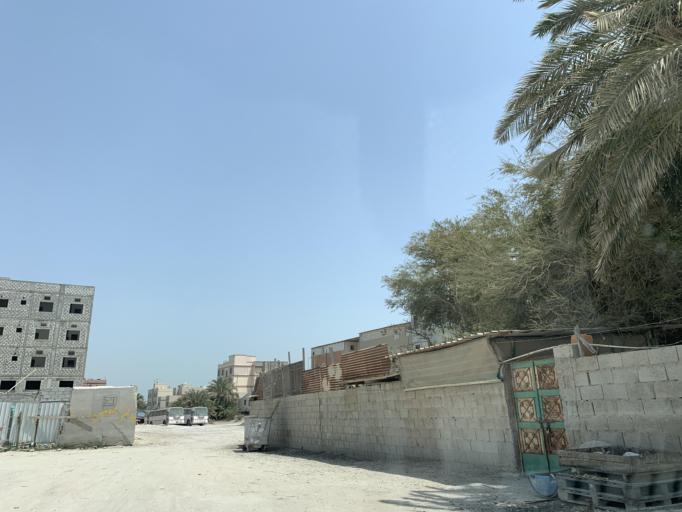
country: BH
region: Northern
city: Madinat `Isa
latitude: 26.1884
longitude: 50.5500
